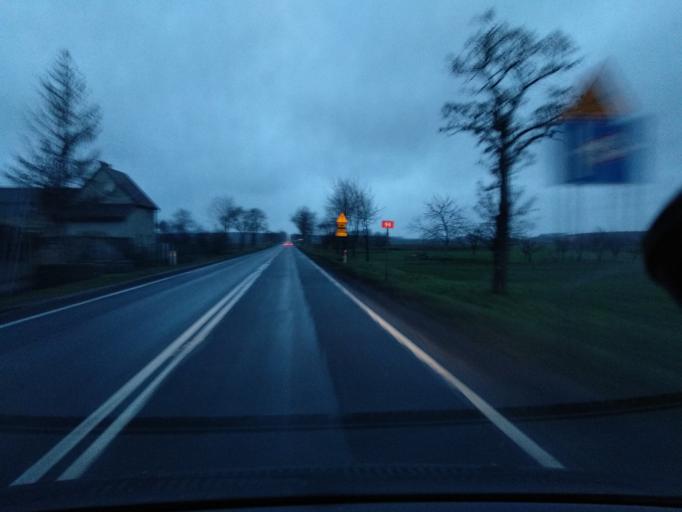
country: PL
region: Lower Silesian Voivodeship
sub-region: Powiat legnicki
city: Prochowice
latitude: 51.2324
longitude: 16.4227
